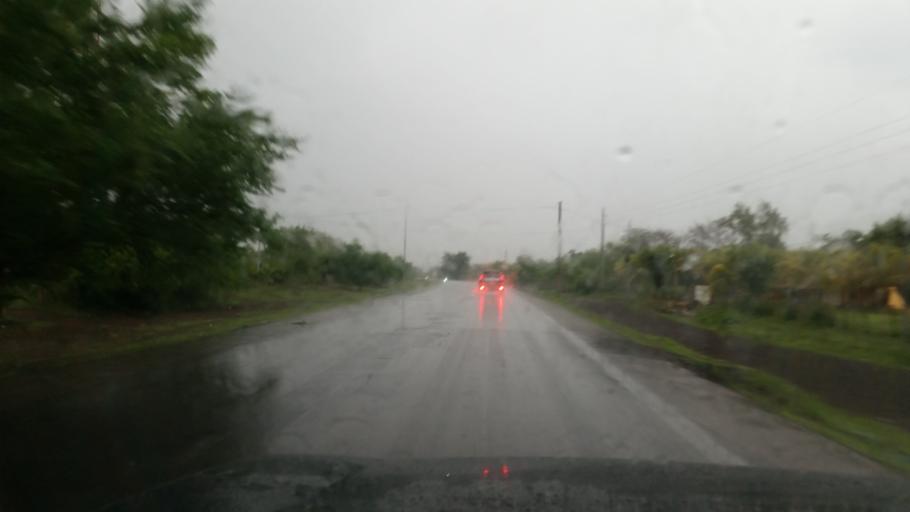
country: NI
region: Chinandega
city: Chichigalpa
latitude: 12.7869
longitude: -86.9430
